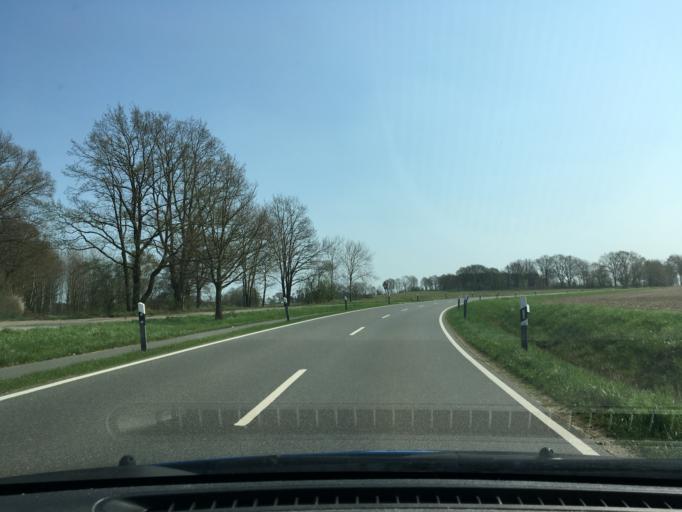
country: DE
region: Lower Saxony
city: Kirchgellersen
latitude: 53.2269
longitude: 10.2962
